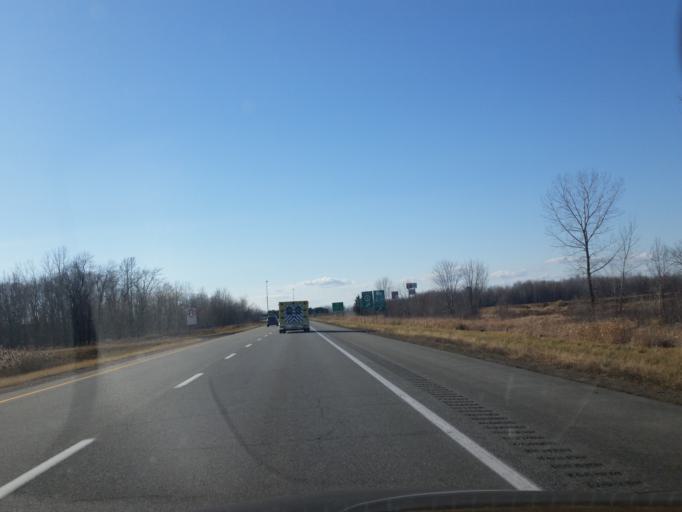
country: CA
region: Quebec
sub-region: Mauricie
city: Yamachiche
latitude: 46.2630
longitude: -72.8642
